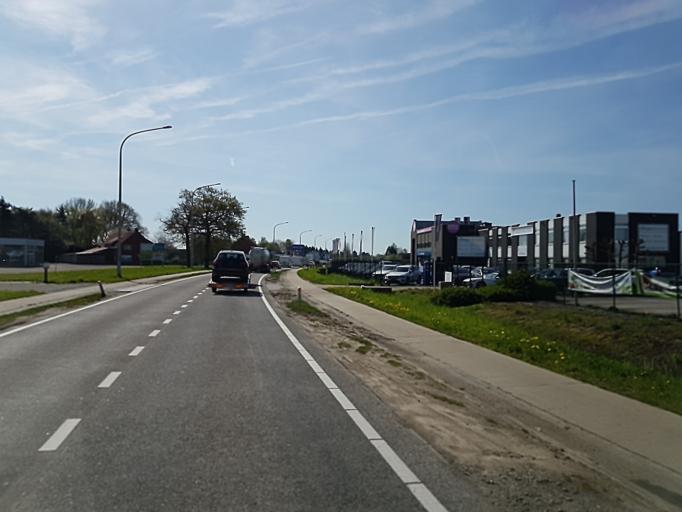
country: BE
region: Flanders
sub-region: Provincie Antwerpen
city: Westerlo
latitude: 51.1251
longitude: 4.9422
